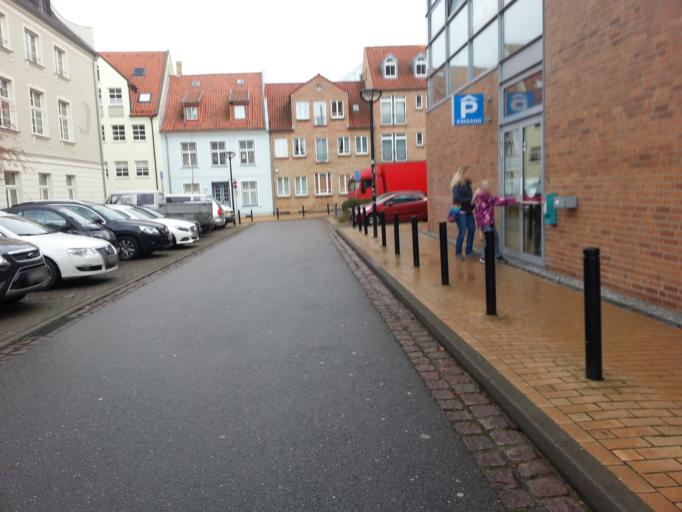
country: DE
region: Mecklenburg-Vorpommern
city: Rostock
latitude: 54.0906
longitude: 12.1363
